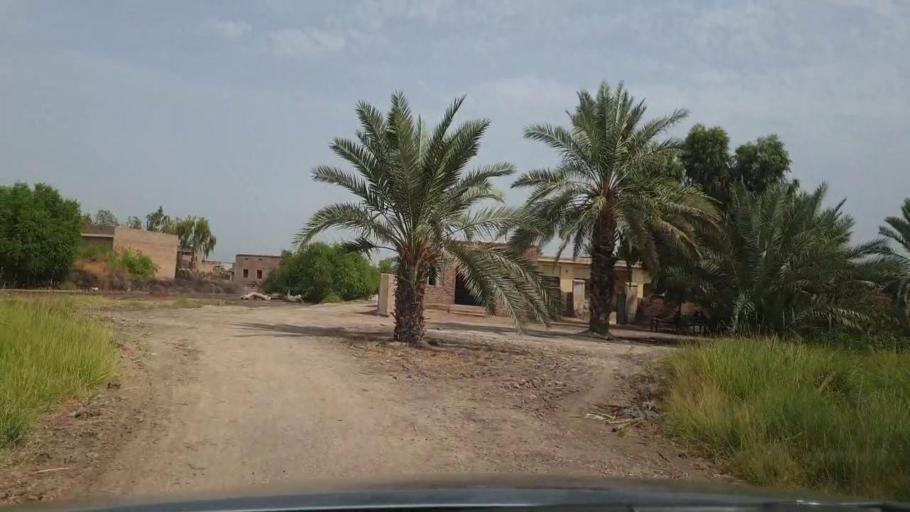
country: PK
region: Sindh
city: Rohri
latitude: 27.6885
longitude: 69.0372
